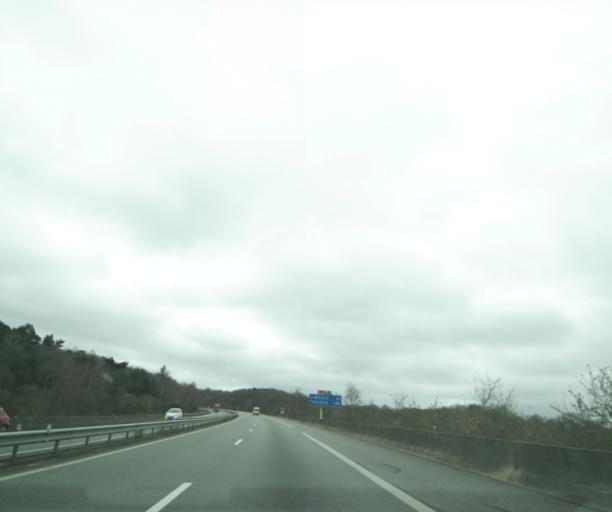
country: FR
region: Limousin
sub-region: Departement de la Haute-Vienne
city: Bessines-sur-Gartempe
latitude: 46.0999
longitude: 1.3649
